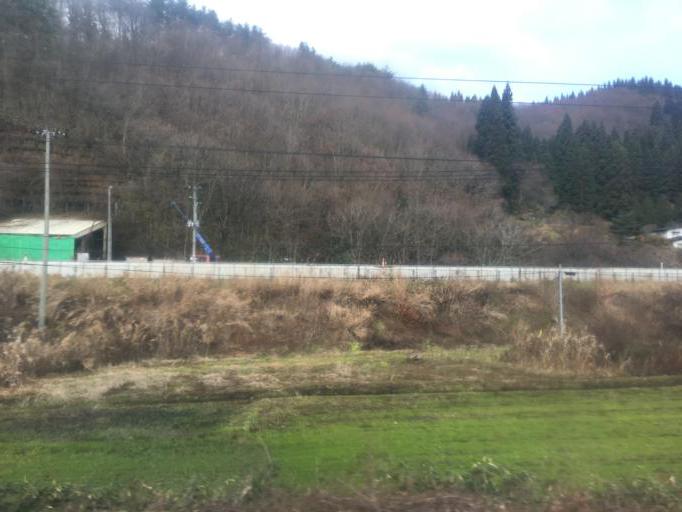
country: JP
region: Akita
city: Takanosu
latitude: 40.2140
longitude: 140.3106
